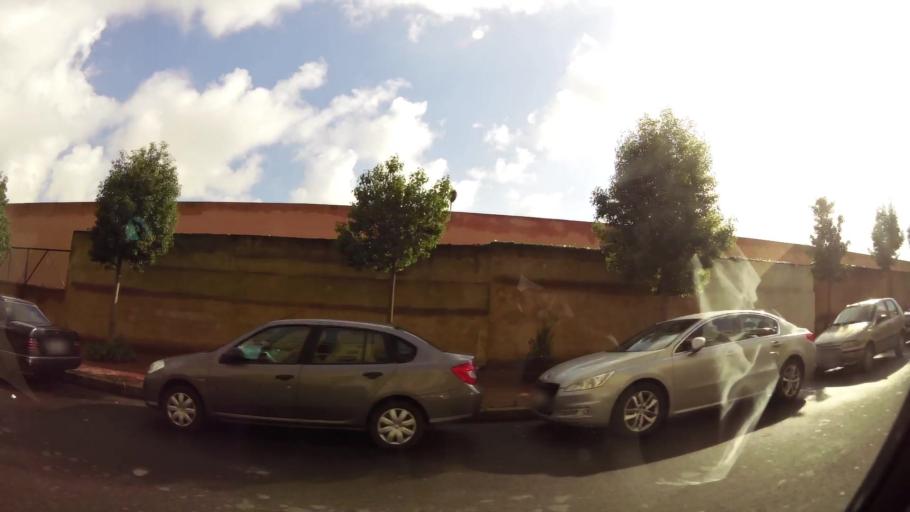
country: MA
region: Grand Casablanca
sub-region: Mediouna
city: Tit Mellil
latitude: 33.5954
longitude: -7.5326
